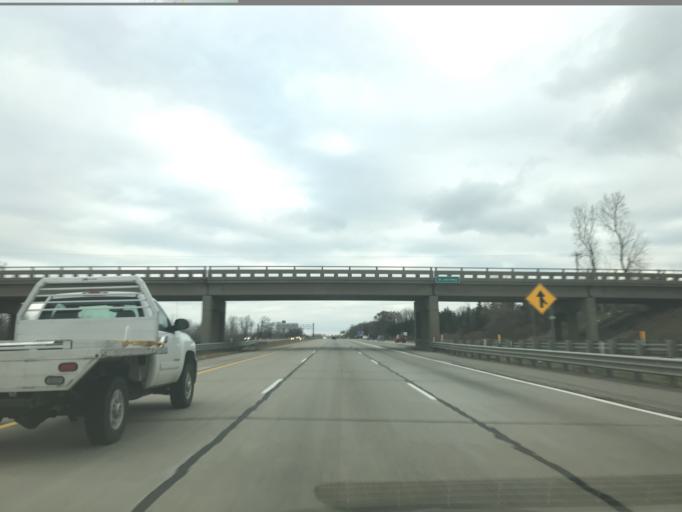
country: US
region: Michigan
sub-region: Eaton County
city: Waverly
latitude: 42.7257
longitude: -84.6686
